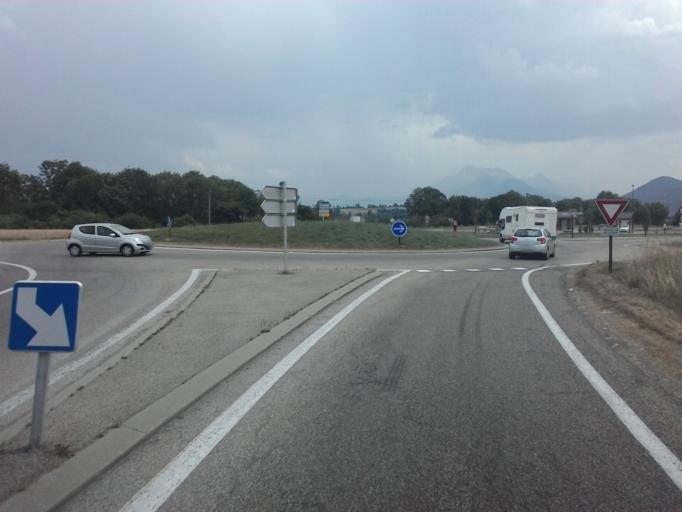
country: FR
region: Rhone-Alpes
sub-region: Departement de l'Isere
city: Pierre-Chatel
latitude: 44.9605
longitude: 5.7798
